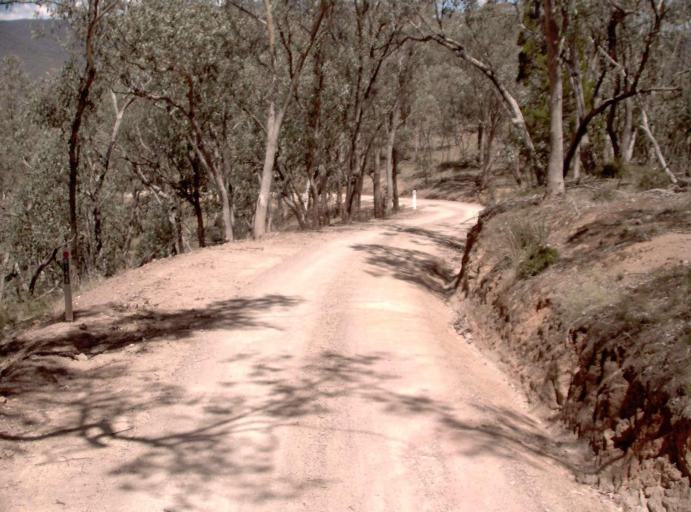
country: AU
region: New South Wales
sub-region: Snowy River
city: Jindabyne
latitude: -37.0906
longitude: 148.3654
